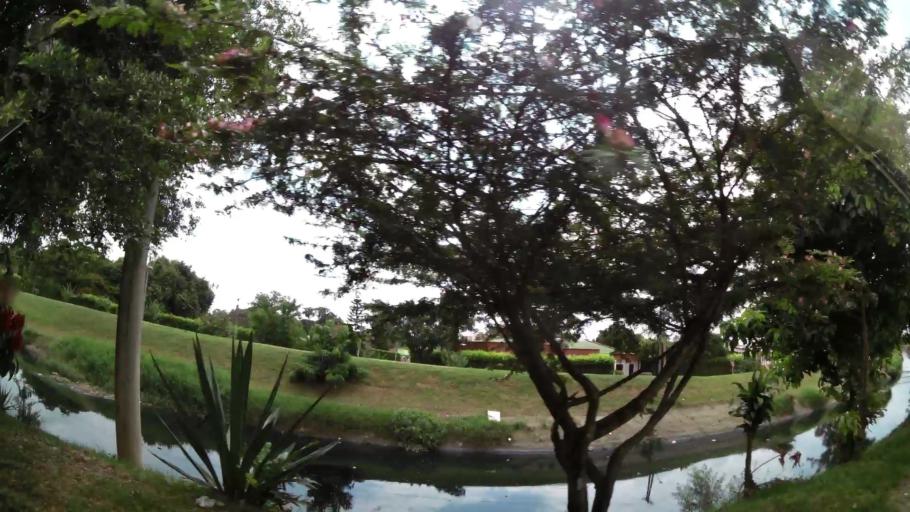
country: CO
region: Valle del Cauca
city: Cali
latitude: 3.4901
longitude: -76.4862
